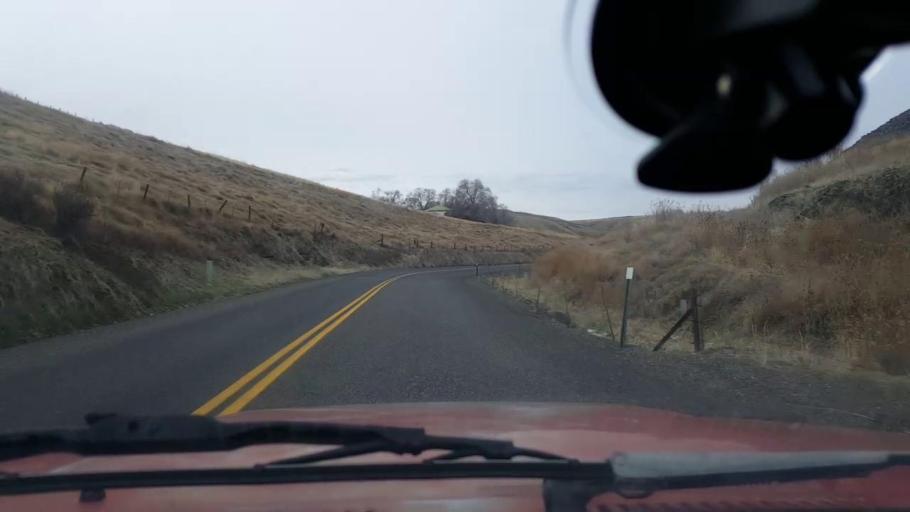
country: US
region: Washington
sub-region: Asotin County
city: Clarkston Heights-Vineland
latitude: 46.3822
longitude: -117.1298
